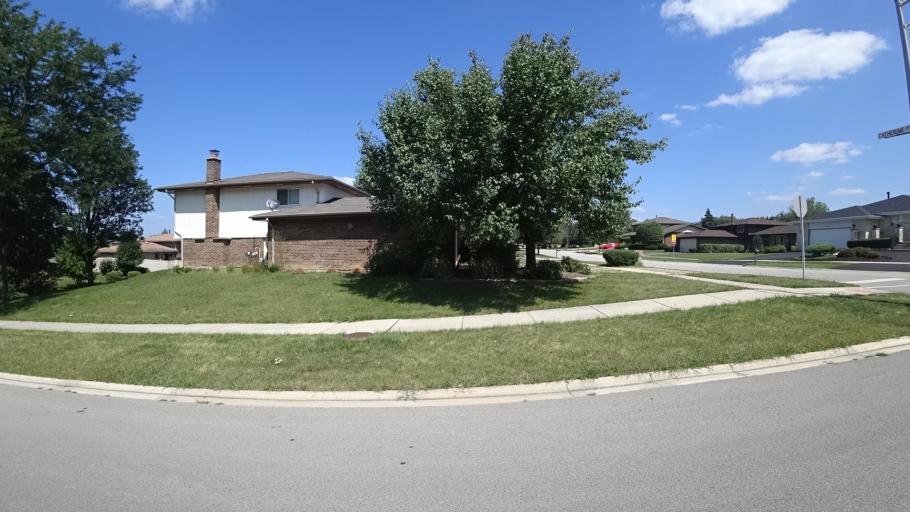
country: US
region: Illinois
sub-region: Cook County
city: Orland Park
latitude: 41.6326
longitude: -87.8464
